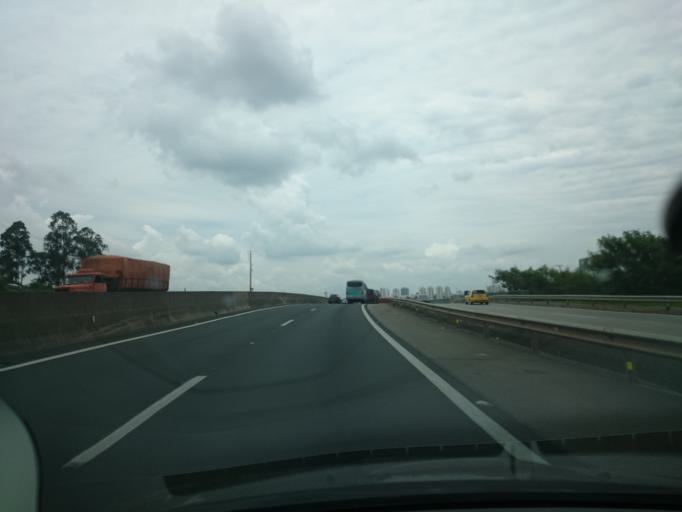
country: BR
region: Sao Paulo
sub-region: Votorantim
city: Votorantim
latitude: -23.5242
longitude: -47.4401
